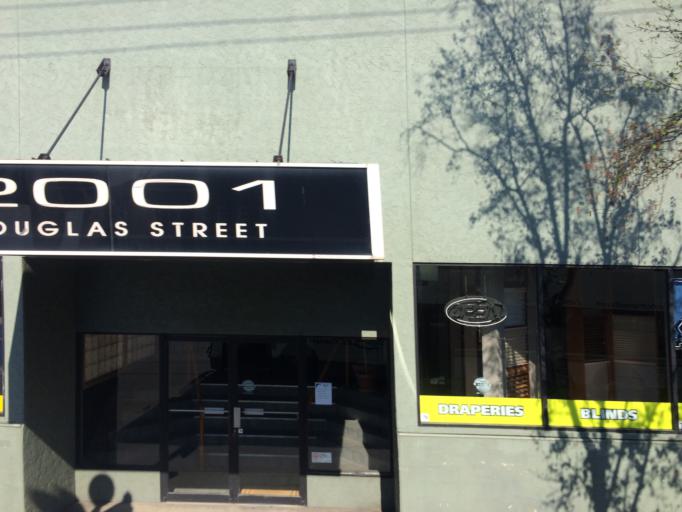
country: CA
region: British Columbia
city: Victoria
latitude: 48.4324
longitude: -123.3645
